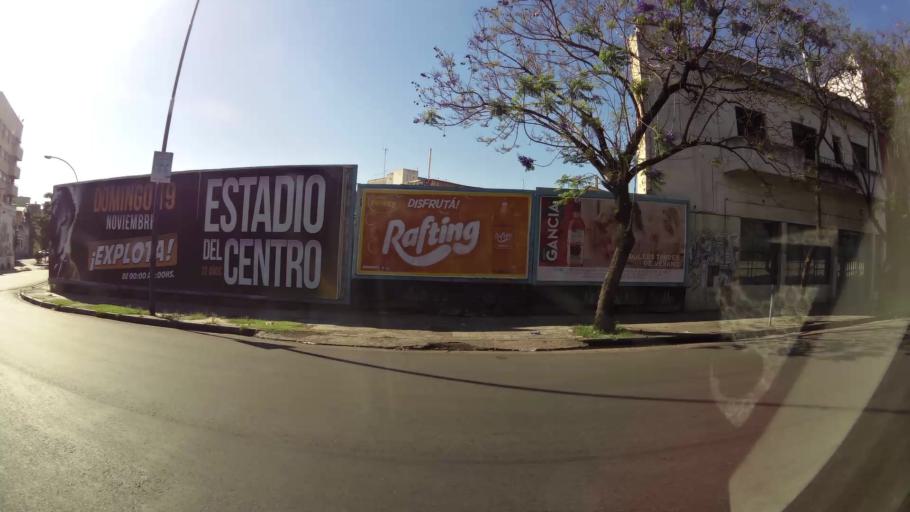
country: AR
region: Cordoba
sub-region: Departamento de Capital
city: Cordoba
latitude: -31.4065
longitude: -64.1823
